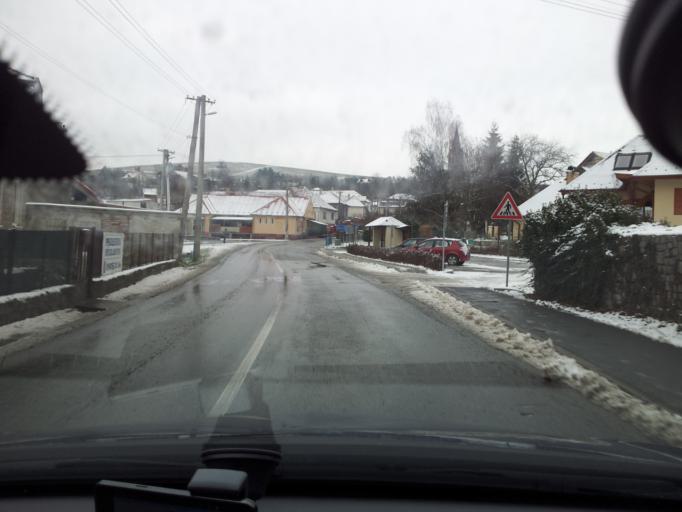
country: SK
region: Presovsky
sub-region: Okres Presov
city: Presov
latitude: 48.8609
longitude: 21.2343
